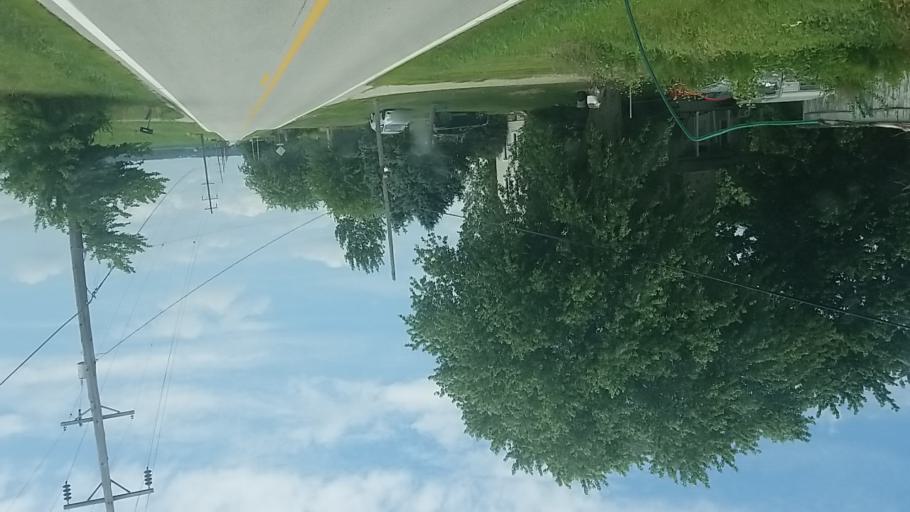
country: US
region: Ohio
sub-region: Franklin County
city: Groveport
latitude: 39.7984
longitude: -82.8896
